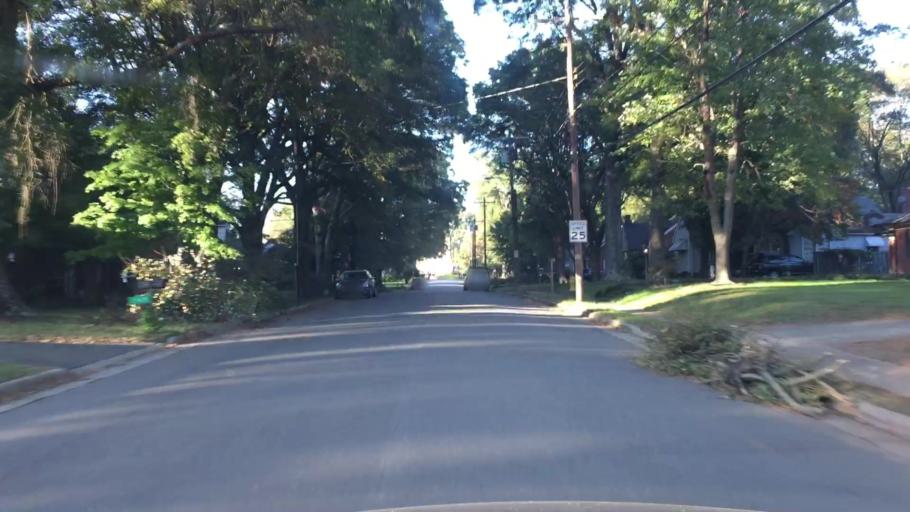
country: US
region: North Carolina
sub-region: Iredell County
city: Mooresville
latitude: 35.5765
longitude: -80.8040
